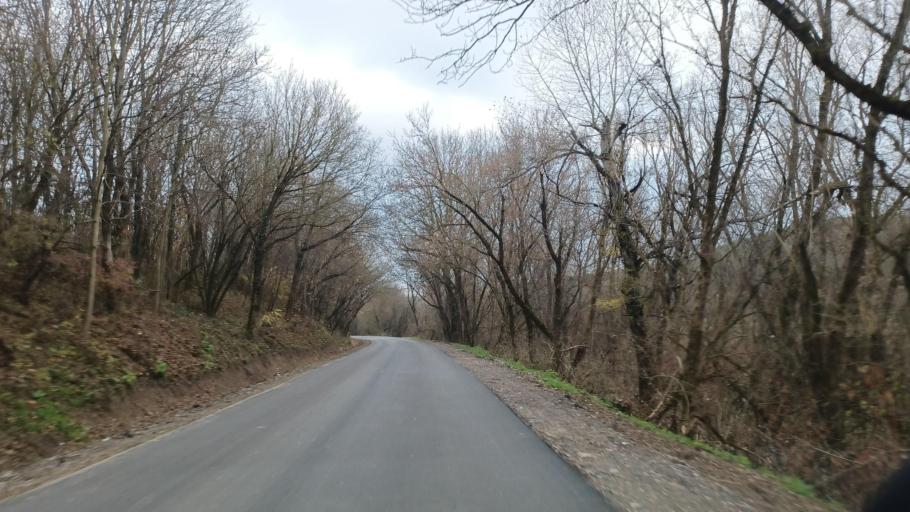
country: HU
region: Tolna
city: Gyonk
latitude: 46.5385
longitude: 18.4967
